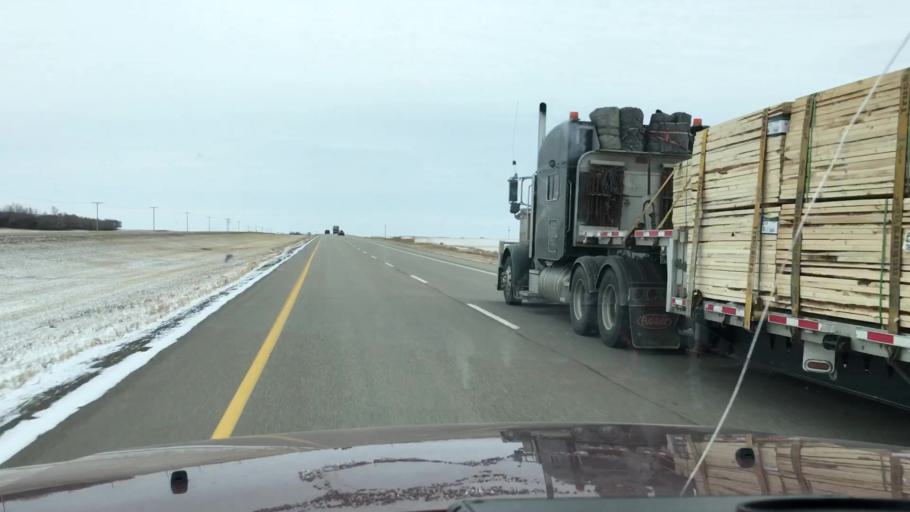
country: CA
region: Saskatchewan
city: Watrous
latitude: 51.2182
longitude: -105.9617
